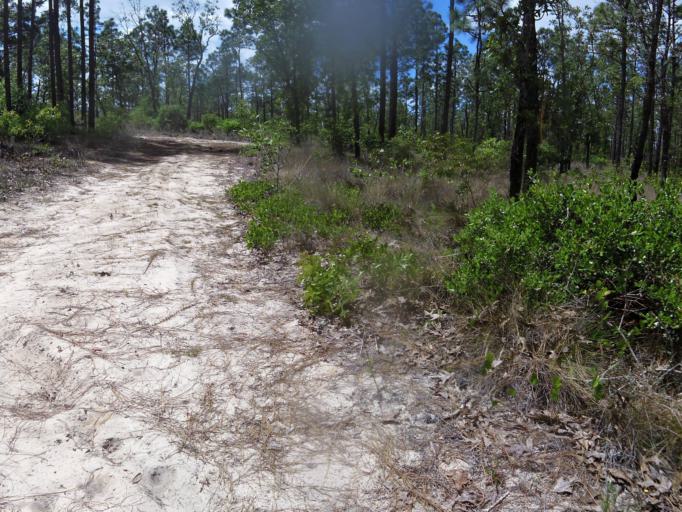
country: US
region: Florida
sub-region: Clay County
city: Keystone Heights
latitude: 29.8404
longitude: -81.9636
